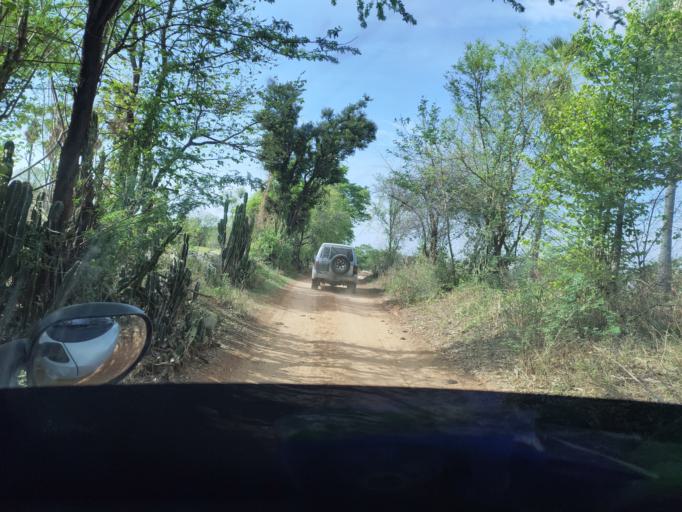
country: MM
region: Magway
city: Chauk
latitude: 20.9566
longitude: 94.9910
